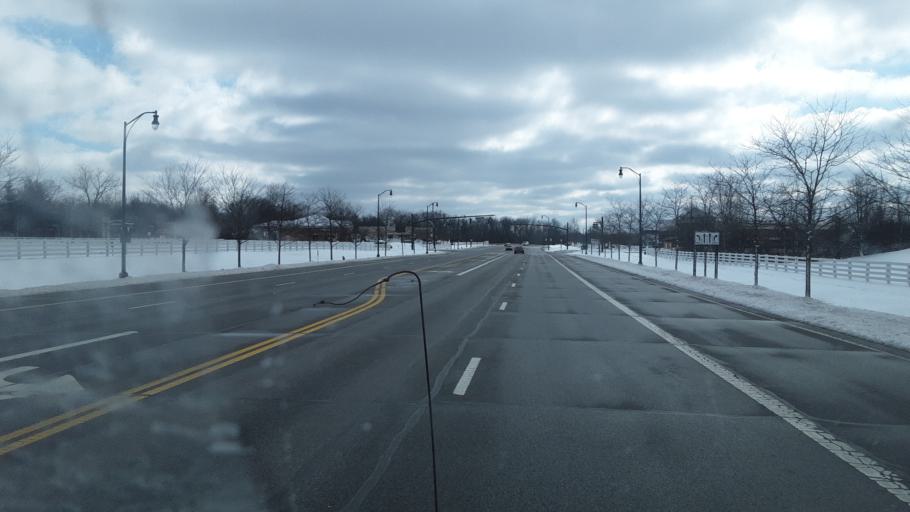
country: US
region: Ohio
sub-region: Franklin County
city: New Albany
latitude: 40.1000
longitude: -82.8174
